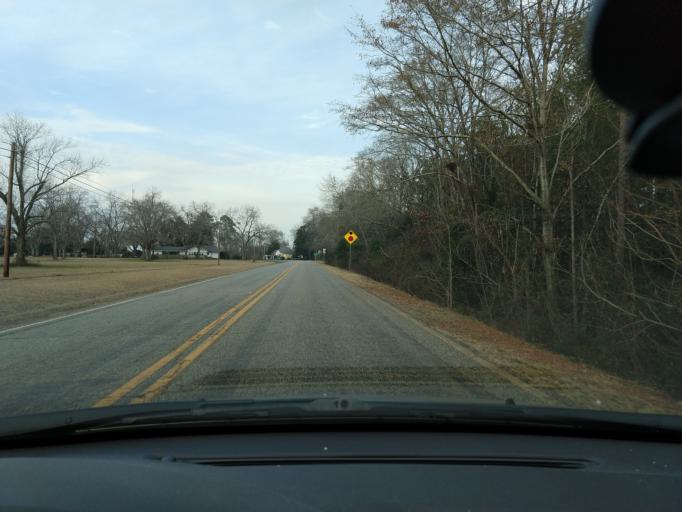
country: US
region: Georgia
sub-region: Webster County
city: Preston
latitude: 32.0283
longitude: -84.3922
